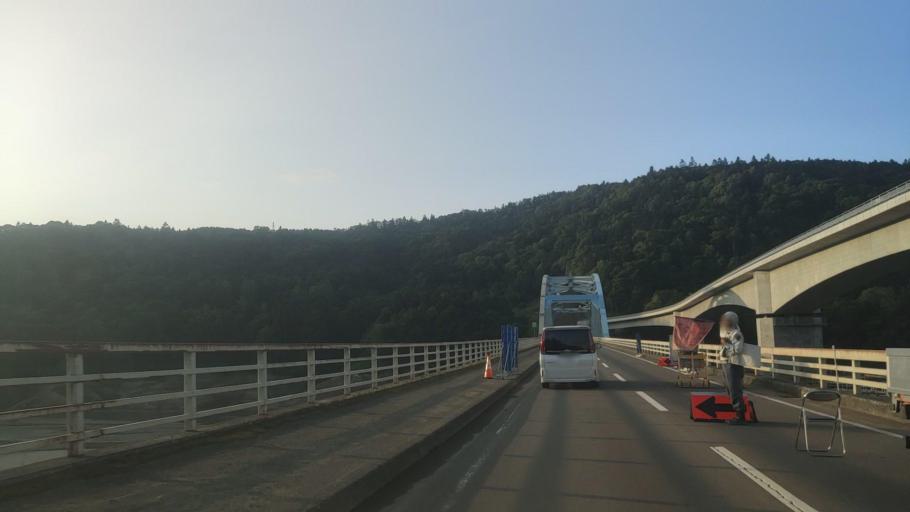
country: JP
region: Hokkaido
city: Bibai
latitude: 43.2343
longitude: 142.0373
